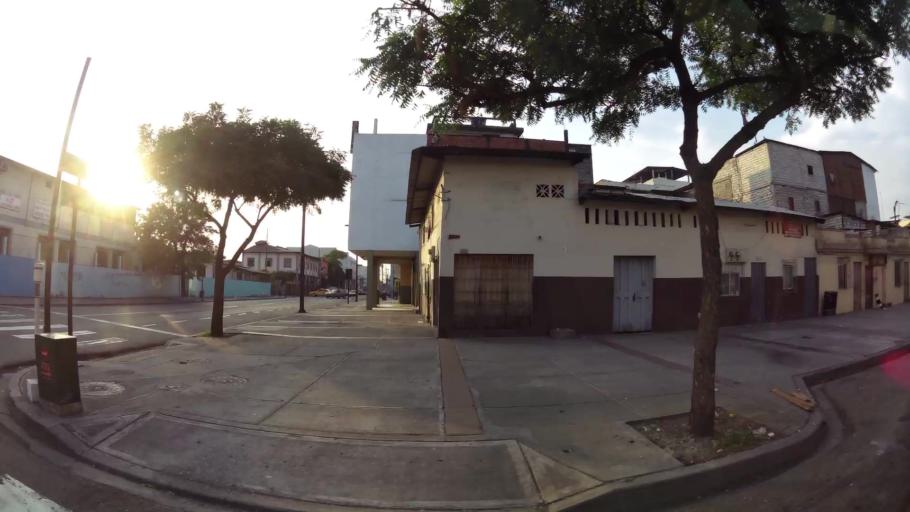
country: EC
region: Guayas
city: Guayaquil
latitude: -2.2001
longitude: -79.8977
